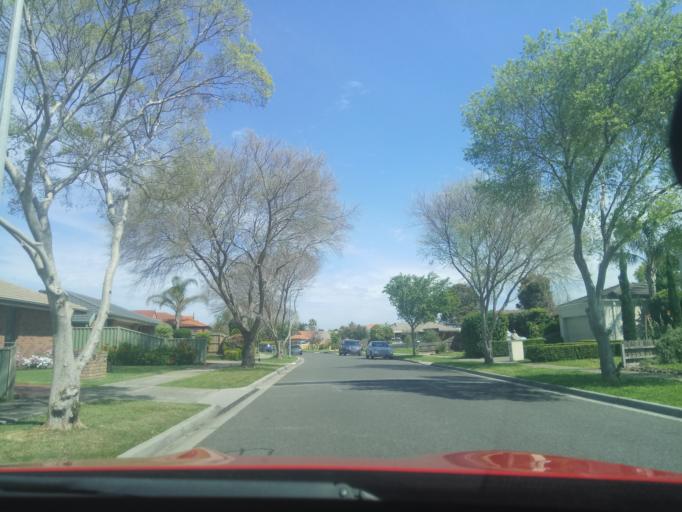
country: AU
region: Victoria
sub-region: Kingston
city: Aspendale Gardens
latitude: -38.0193
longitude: 145.1155
